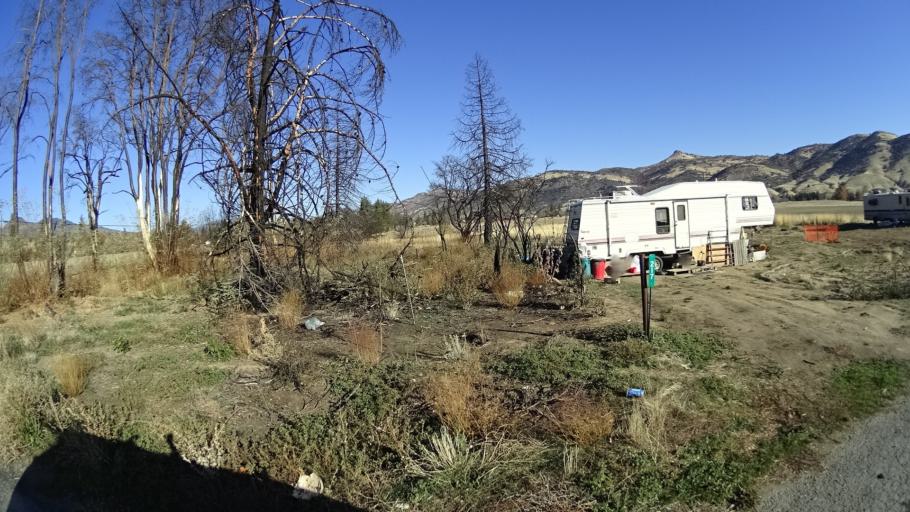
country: US
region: California
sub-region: Siskiyou County
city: Montague
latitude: 41.9031
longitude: -122.5626
